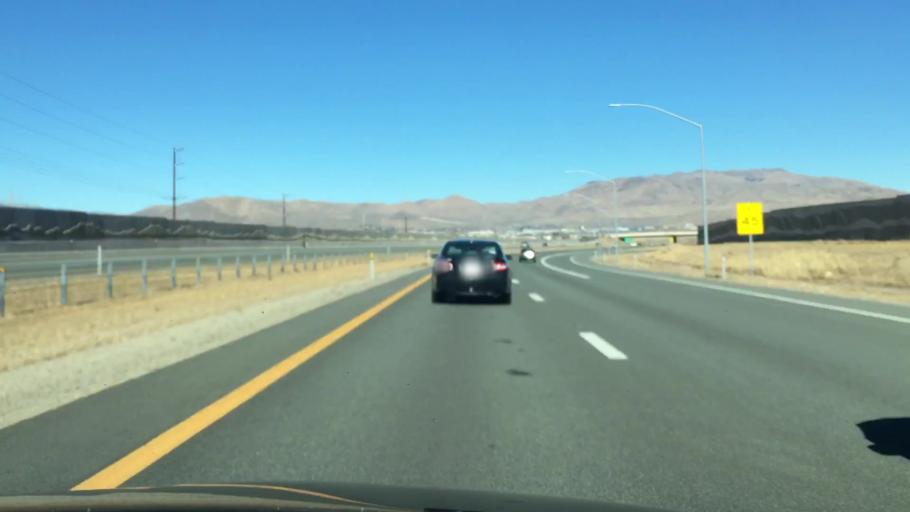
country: US
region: Nevada
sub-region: Carson City
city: Carson City
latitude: 39.1446
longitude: -119.7466
